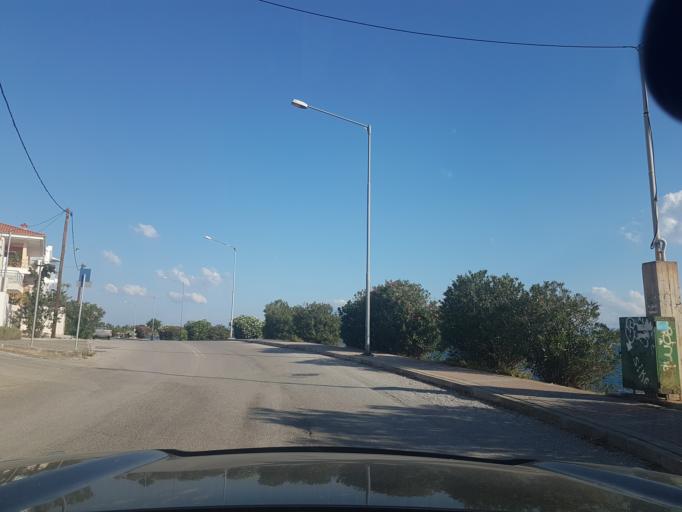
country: GR
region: Central Greece
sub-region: Nomos Evvoias
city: Chalkida
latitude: 38.4749
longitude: 23.5910
